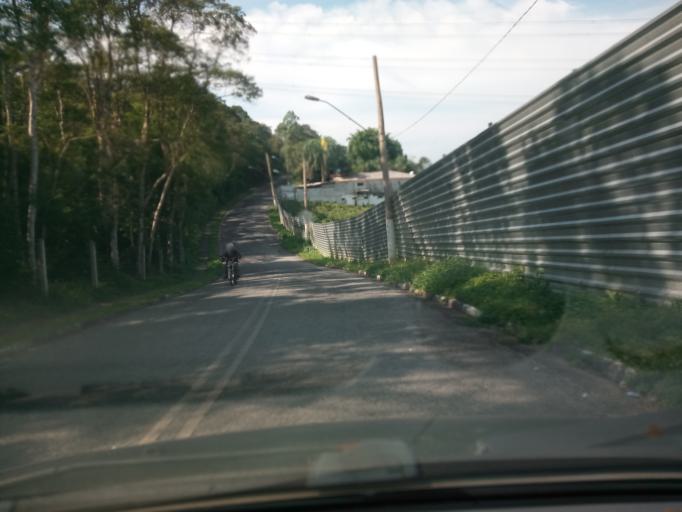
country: BR
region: Sao Paulo
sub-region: Sao Bernardo Do Campo
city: Sao Bernardo do Campo
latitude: -23.7958
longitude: -46.5393
